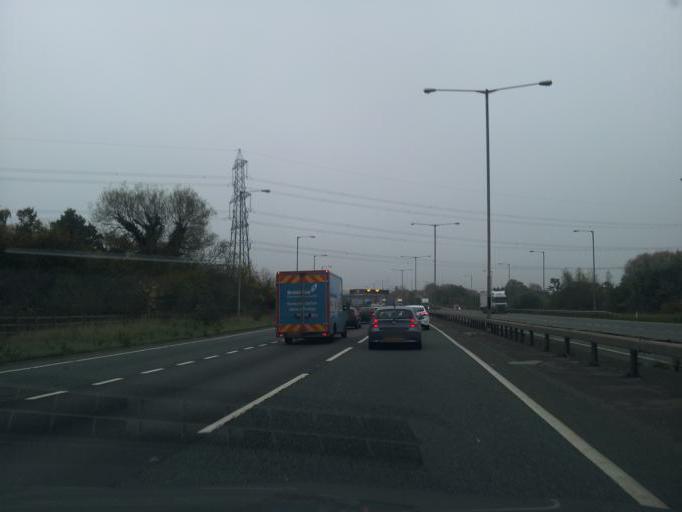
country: GB
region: England
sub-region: Leicestershire
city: Kirby Muxloe
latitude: 52.6481
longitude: -1.2225
